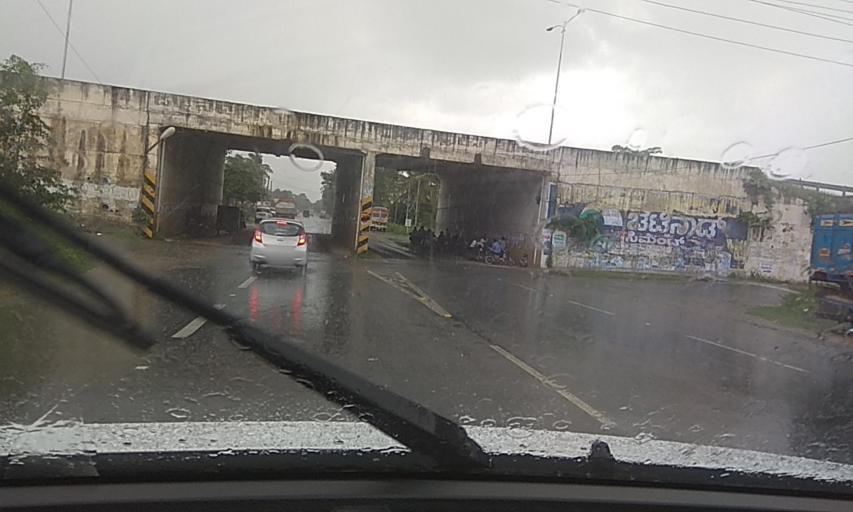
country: IN
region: Karnataka
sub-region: Tumkur
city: Kunigal
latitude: 13.0009
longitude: 77.0229
